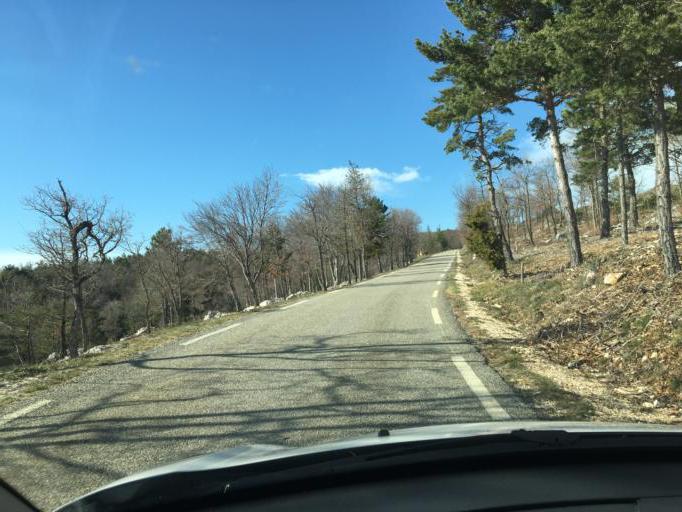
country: FR
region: Provence-Alpes-Cote d'Azur
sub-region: Departement du Vaucluse
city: Saint-Saturnin-les-Apt
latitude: 43.9699
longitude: 5.4620
